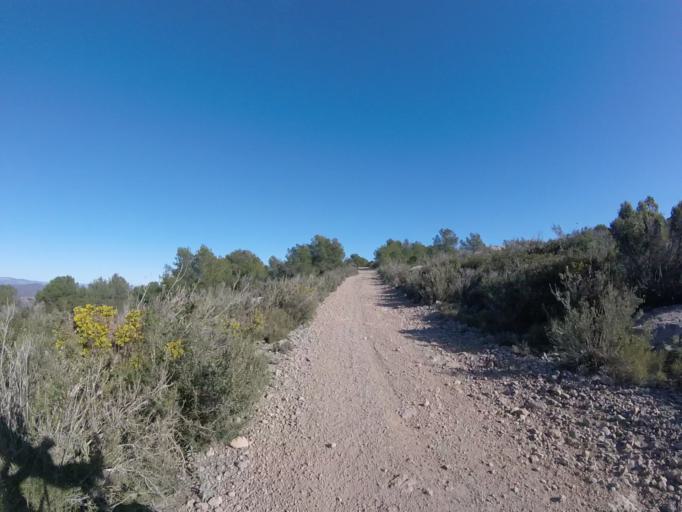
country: ES
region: Valencia
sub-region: Provincia de Castello
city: Orpesa/Oropesa del Mar
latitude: 40.0997
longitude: 0.1110
